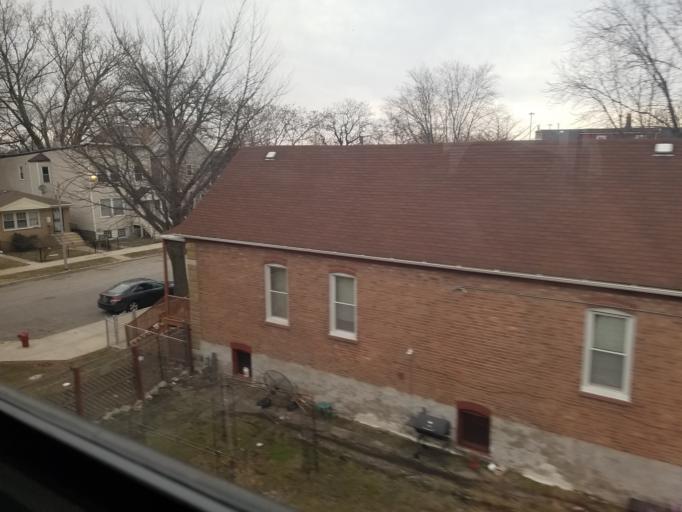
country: US
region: Illinois
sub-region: Cook County
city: Chicago
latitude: 41.7881
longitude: -87.6351
